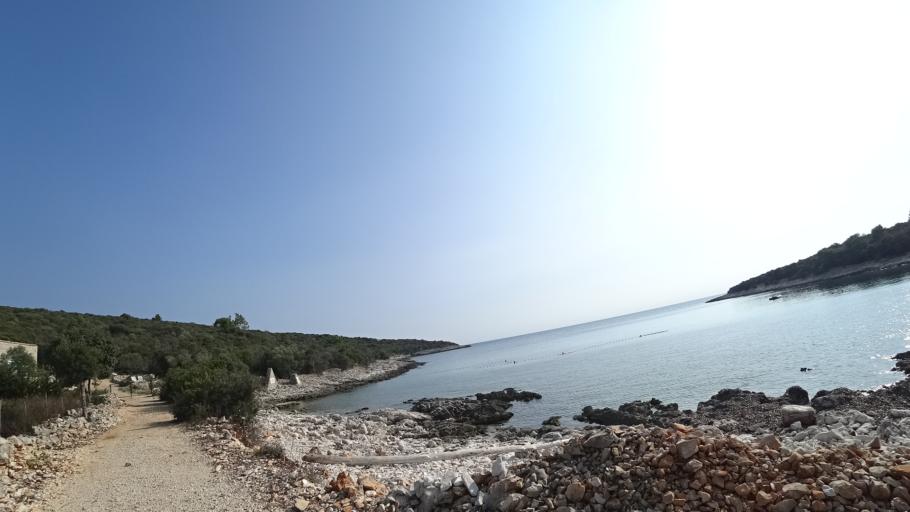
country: HR
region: Primorsko-Goranska
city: Mali Losinj
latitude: 44.4887
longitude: 14.5074
